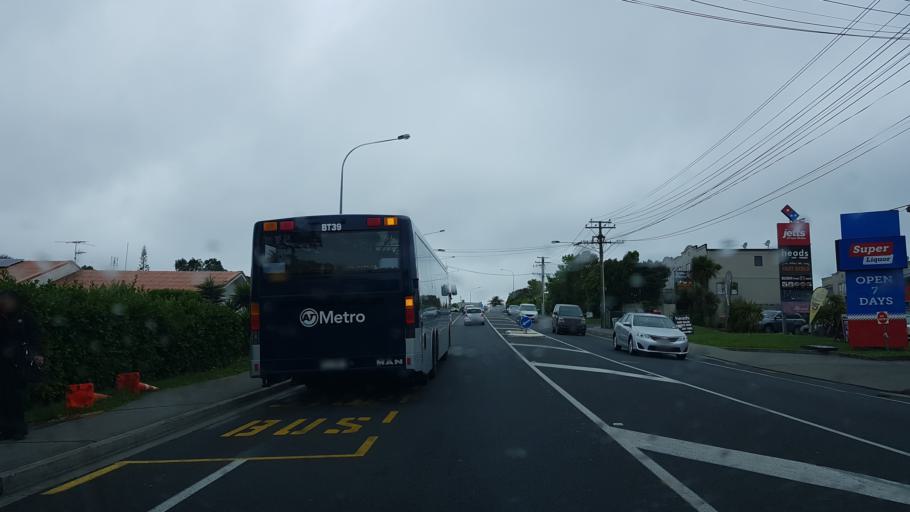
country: NZ
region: Auckland
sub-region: Auckland
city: North Shore
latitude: -36.8108
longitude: 174.7126
